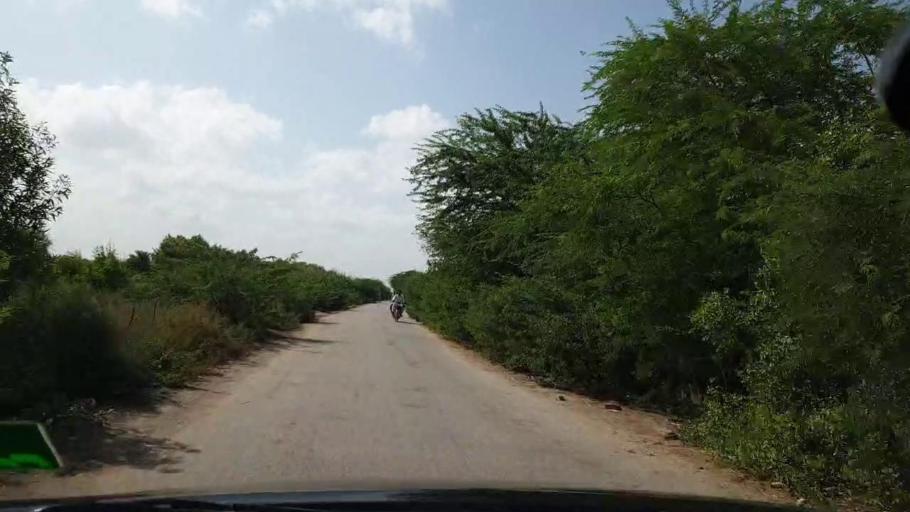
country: PK
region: Sindh
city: Kadhan
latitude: 24.6379
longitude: 69.1157
